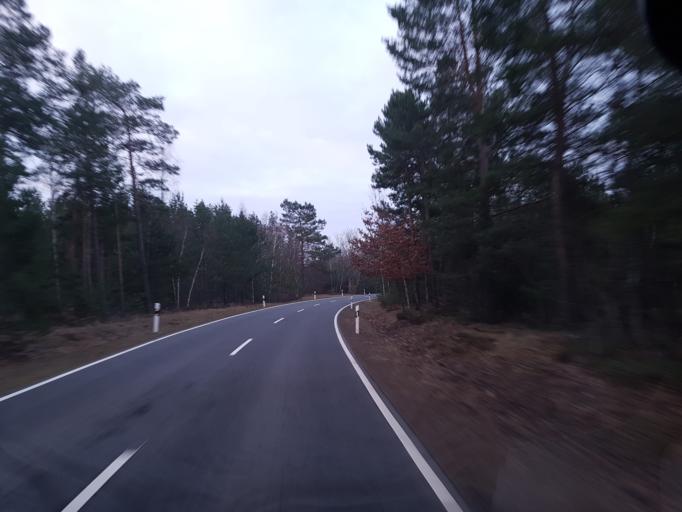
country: DE
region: Brandenburg
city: Sallgast
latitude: 51.5812
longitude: 13.8206
